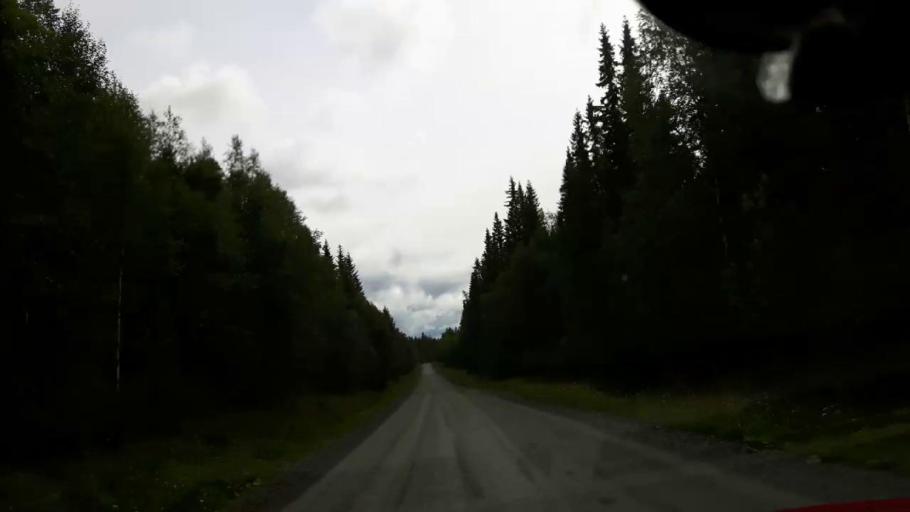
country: SE
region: Jaemtland
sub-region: Krokoms Kommun
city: Valla
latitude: 63.6606
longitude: 13.9704
